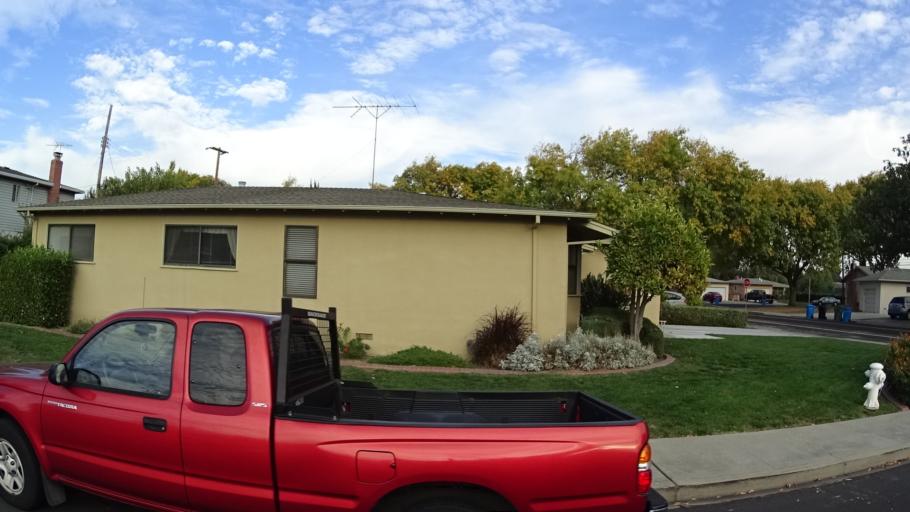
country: US
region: California
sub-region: Santa Clara County
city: Santa Clara
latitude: 37.3372
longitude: -121.9626
